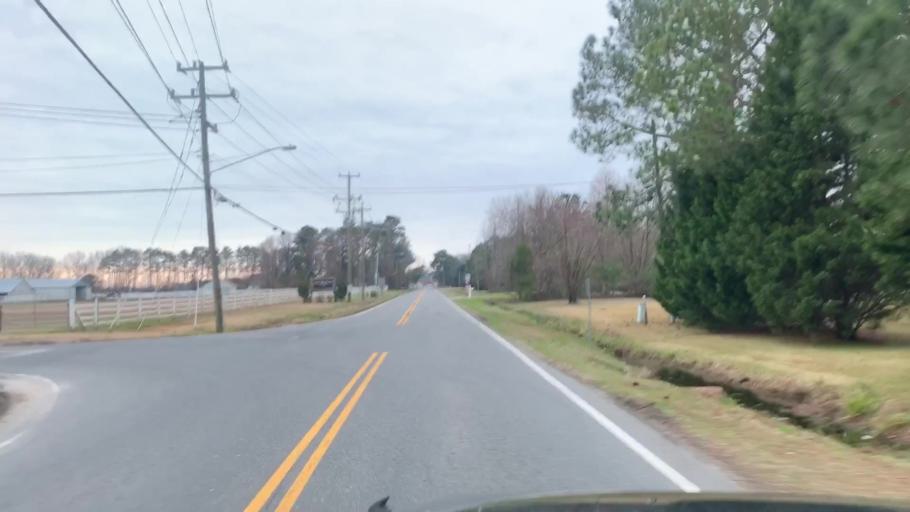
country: US
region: North Carolina
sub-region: Currituck County
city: Moyock
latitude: 36.6407
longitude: -76.2043
